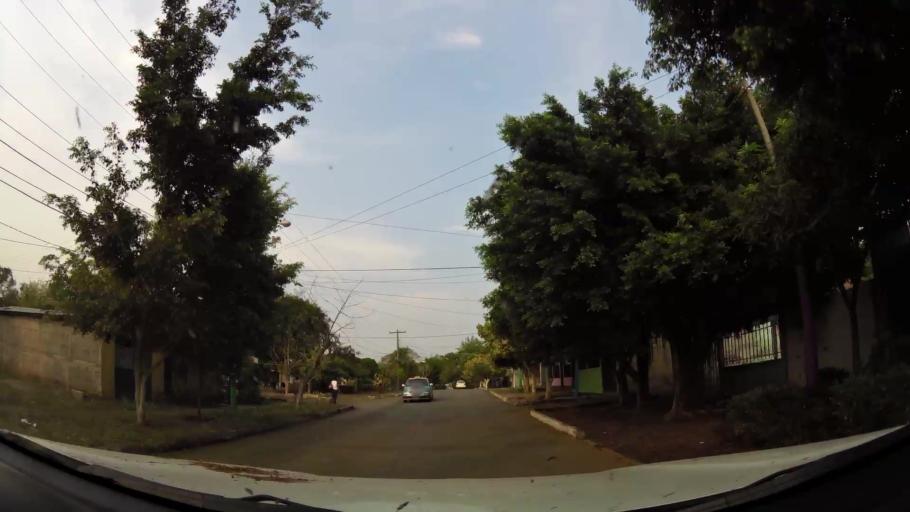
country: NI
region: Masaya
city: Masaya
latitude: 11.9805
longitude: -86.0783
